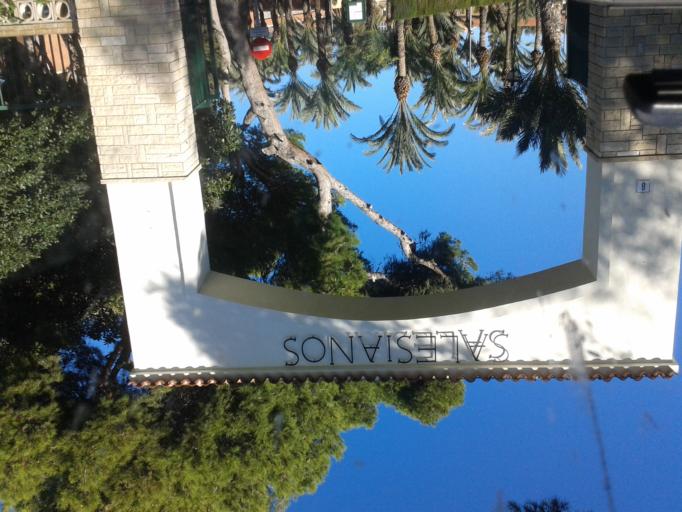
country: ES
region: Valencia
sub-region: Provincia de Alicante
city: el Campello
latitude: 38.4152
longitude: -0.3992
